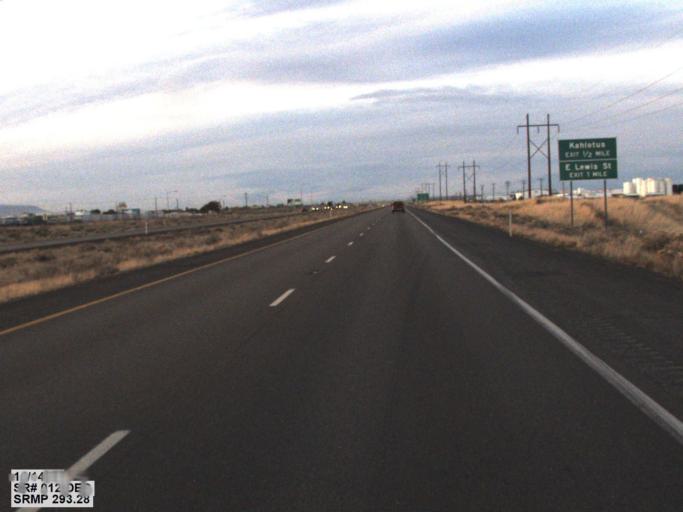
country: US
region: Washington
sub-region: Walla Walla County
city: Burbank
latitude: 46.2305
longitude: -119.0436
